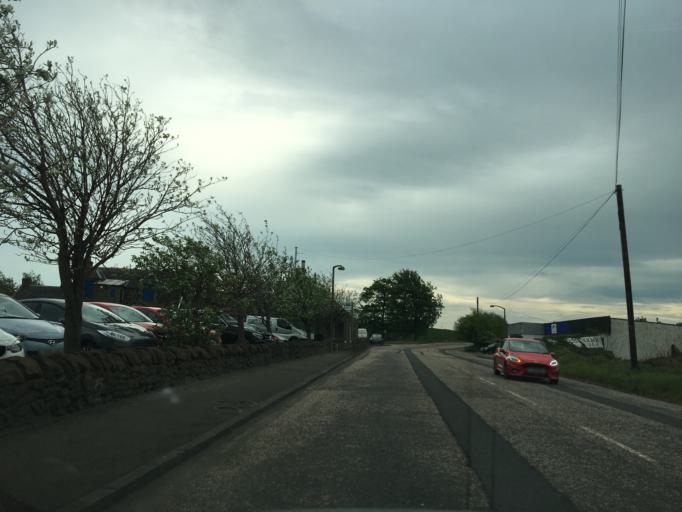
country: GB
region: Scotland
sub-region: Edinburgh
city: Ratho
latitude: 55.9500
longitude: -3.3354
